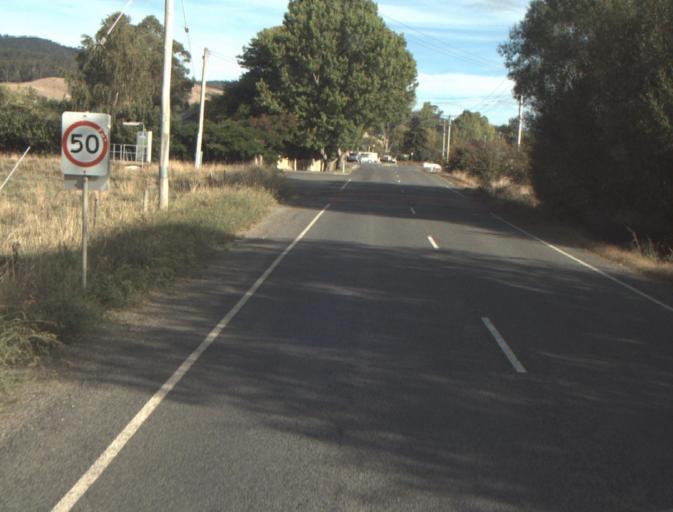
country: AU
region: Tasmania
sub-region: Launceston
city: Mayfield
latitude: -41.2474
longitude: 147.2176
